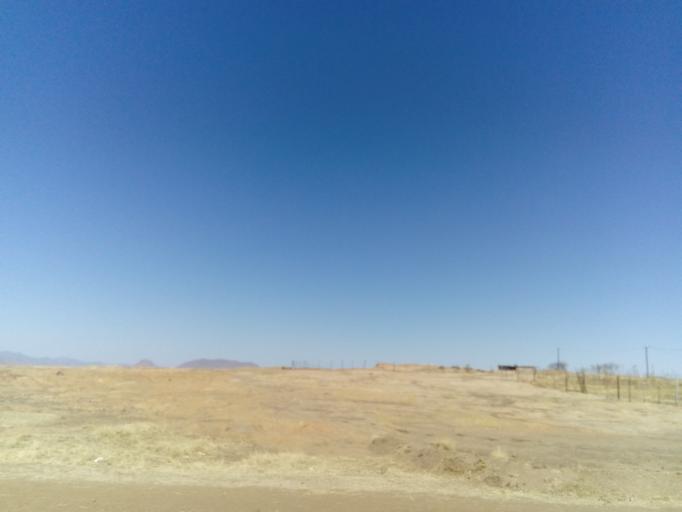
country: LS
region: Berea
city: Teyateyaneng
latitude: -29.1357
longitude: 27.8556
